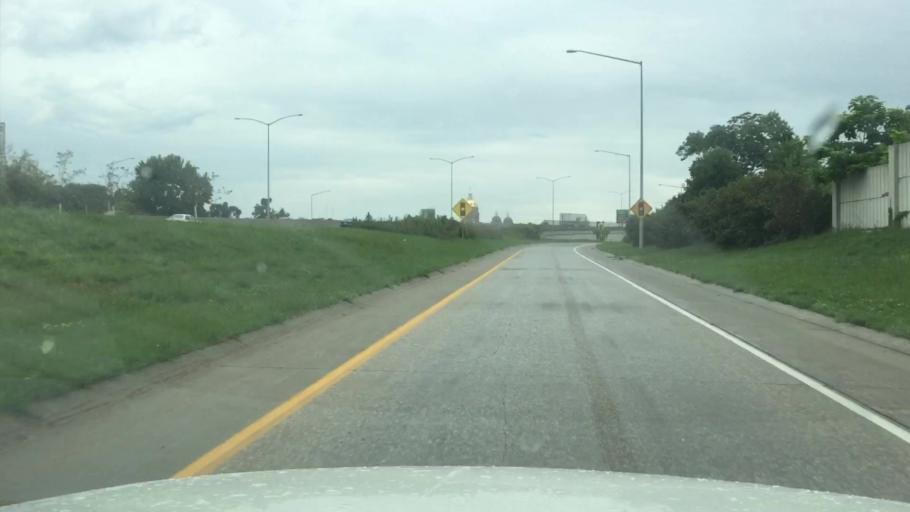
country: US
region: Iowa
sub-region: Polk County
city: Des Moines
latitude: 41.5982
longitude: -93.5923
